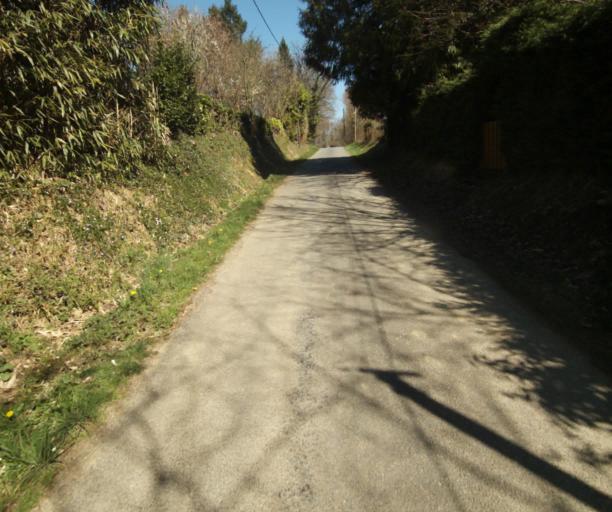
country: FR
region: Limousin
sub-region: Departement de la Correze
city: Saint-Mexant
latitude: 45.3169
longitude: 1.6572
